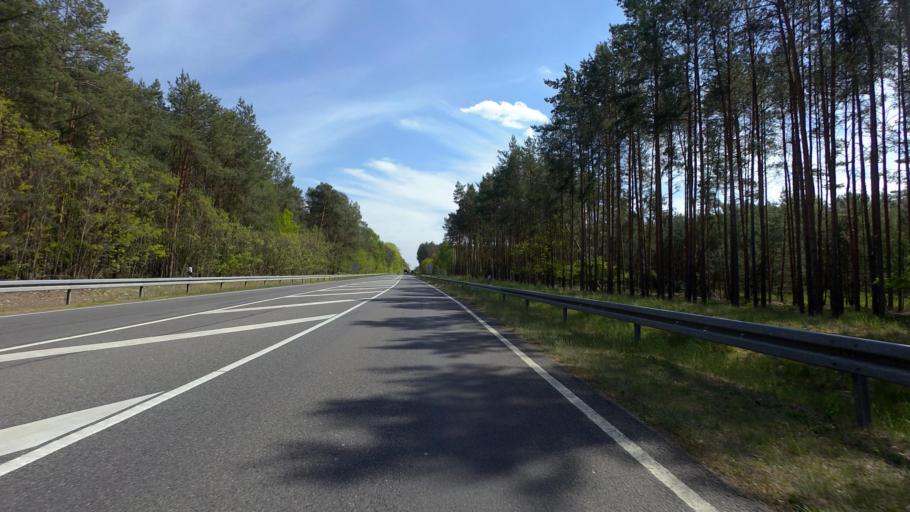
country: DE
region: Brandenburg
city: Heinersbruck
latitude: 51.6947
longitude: 14.4935
